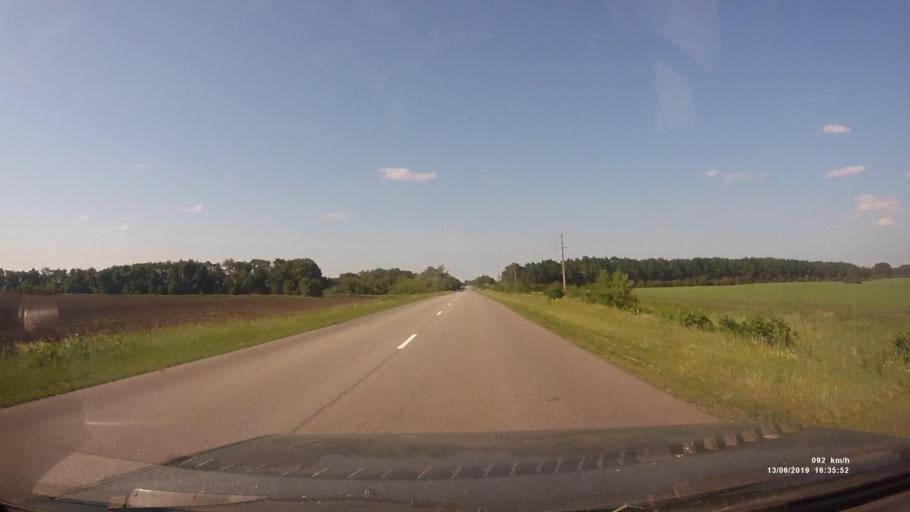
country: RU
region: Rostov
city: Kazanskaya
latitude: 49.8877
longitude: 41.3016
